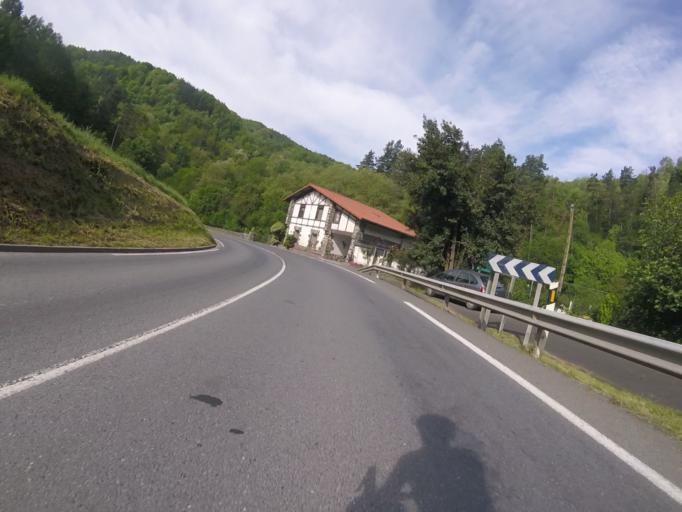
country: ES
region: Basque Country
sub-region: Provincia de Guipuzcoa
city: Urretxu
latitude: 43.1128
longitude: -2.3243
